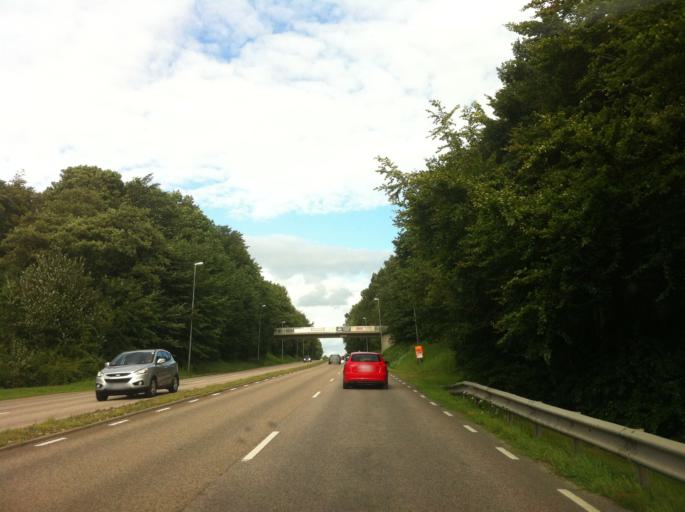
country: SE
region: Skane
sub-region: Bastads Kommun
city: Bastad
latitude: 56.3837
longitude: 12.9147
